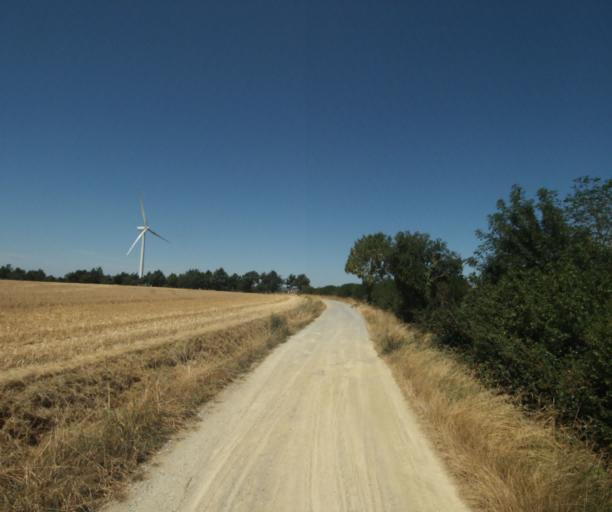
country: FR
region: Midi-Pyrenees
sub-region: Departement de la Haute-Garonne
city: Saint-Felix-Lauragais
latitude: 43.4680
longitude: 1.9203
